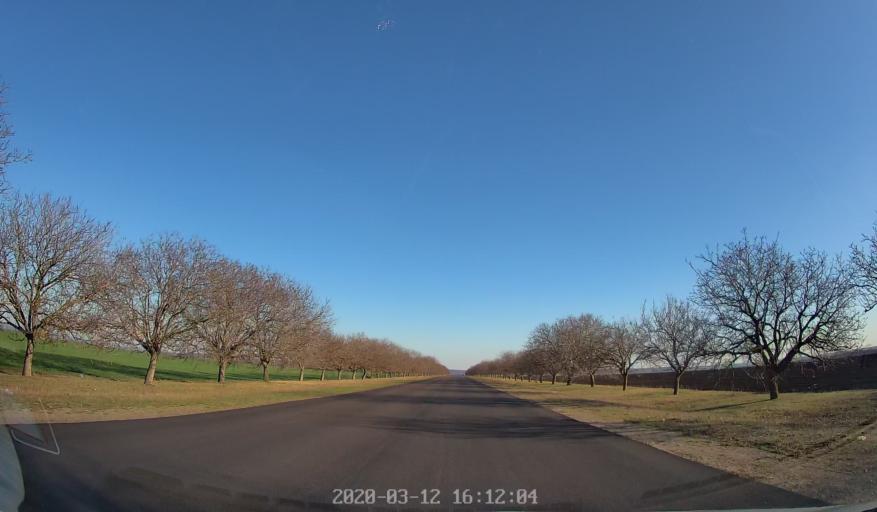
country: MD
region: Anenii Noi
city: Anenii Noi
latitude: 46.9403
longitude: 29.2676
